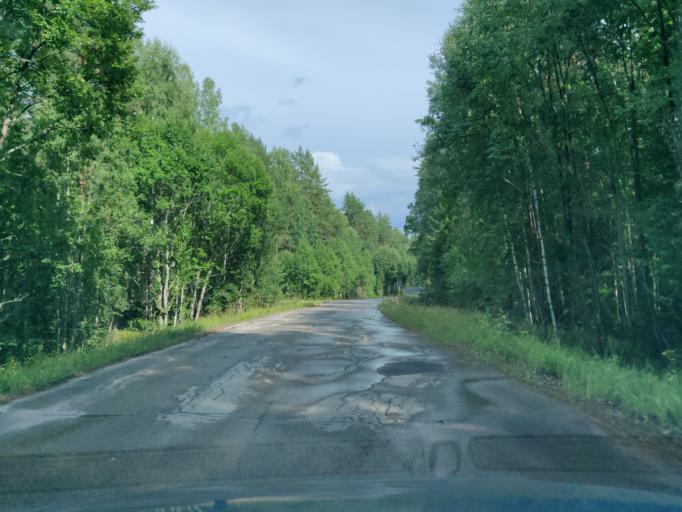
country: SE
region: Vaermland
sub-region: Munkfors Kommun
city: Munkfors
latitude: 59.9731
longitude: 13.5470
